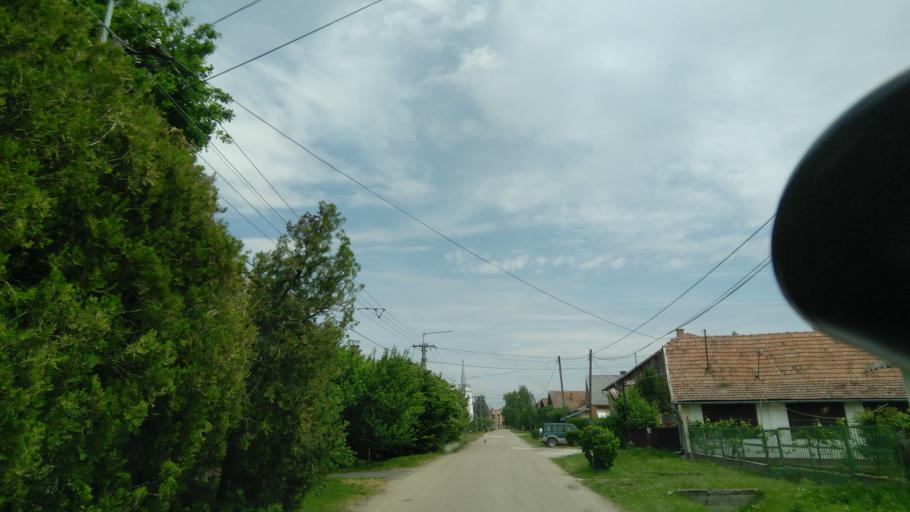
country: HU
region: Bekes
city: Fuzesgyarmat
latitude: 47.1075
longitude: 21.2070
